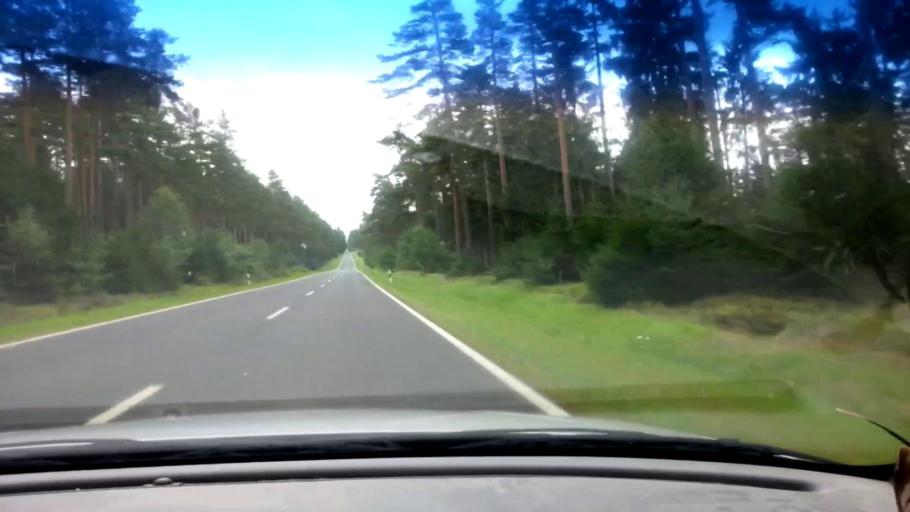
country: DE
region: Bavaria
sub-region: Upper Franconia
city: Schirnding
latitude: 50.0692
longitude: 12.2435
